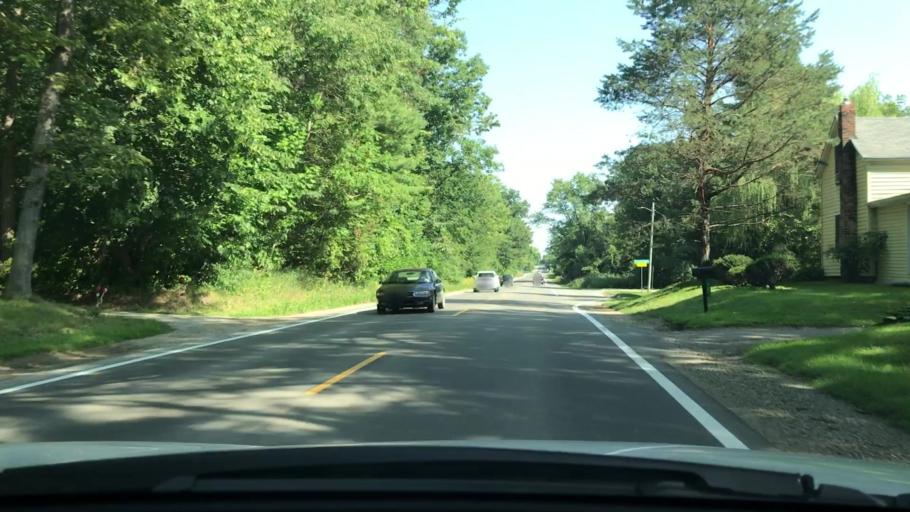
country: US
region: Michigan
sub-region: Oakland County
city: Oxford
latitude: 42.7914
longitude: -83.3328
